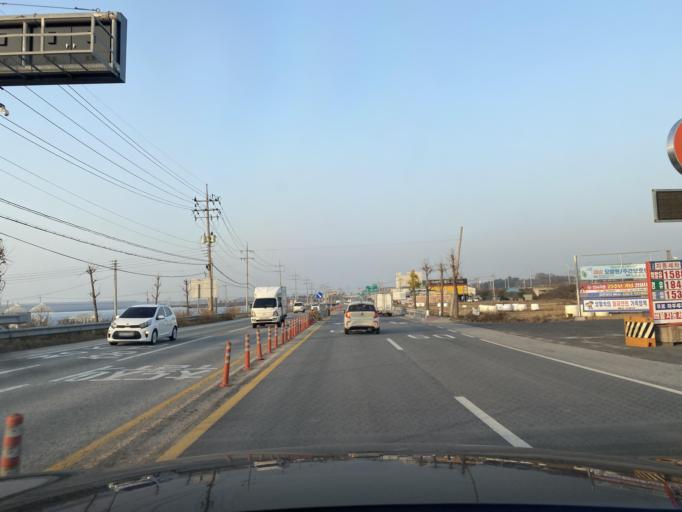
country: KR
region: Chungcheongnam-do
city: Yesan
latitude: 36.6965
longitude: 126.8286
